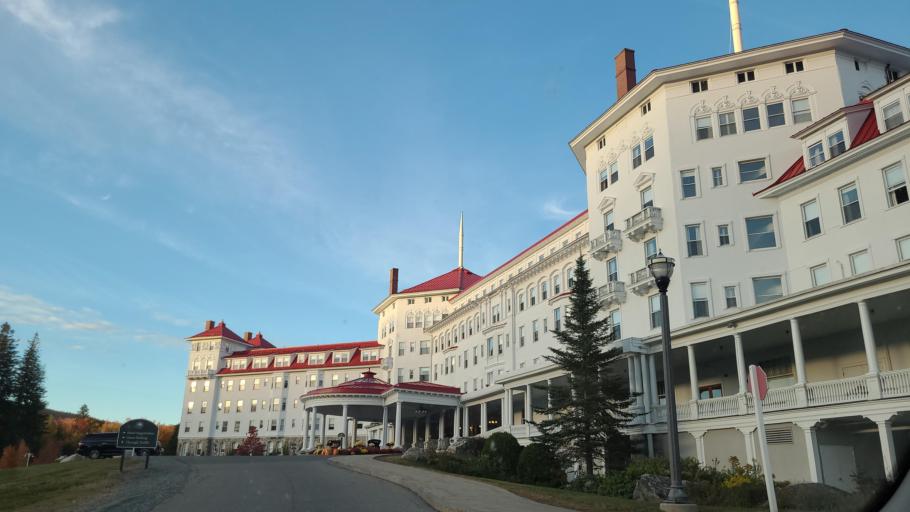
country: US
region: New Hampshire
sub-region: Coos County
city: Jefferson
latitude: 44.2567
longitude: -71.4398
